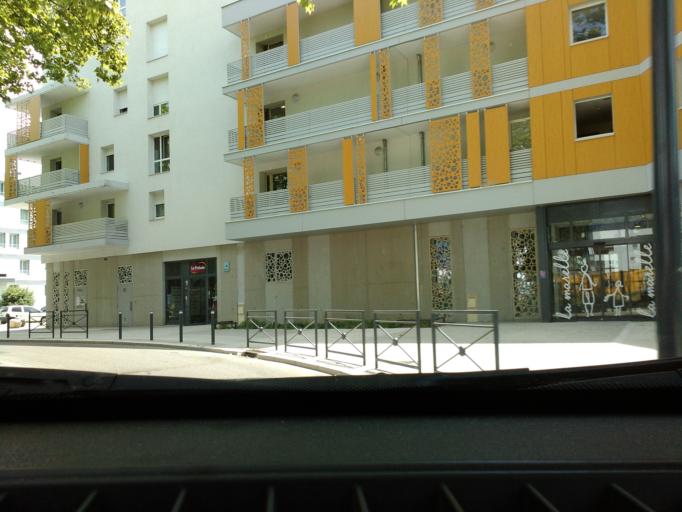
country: FR
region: Rhone-Alpes
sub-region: Departement de l'Isere
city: Saint-Martin-d'Heres
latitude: 45.1782
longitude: 5.7468
